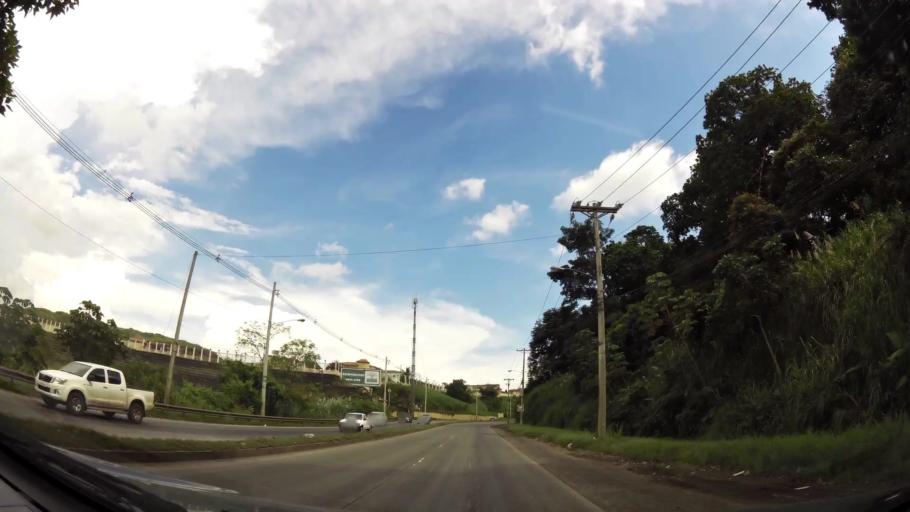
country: PA
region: Panama
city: Panama
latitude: 9.0388
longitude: -79.5447
